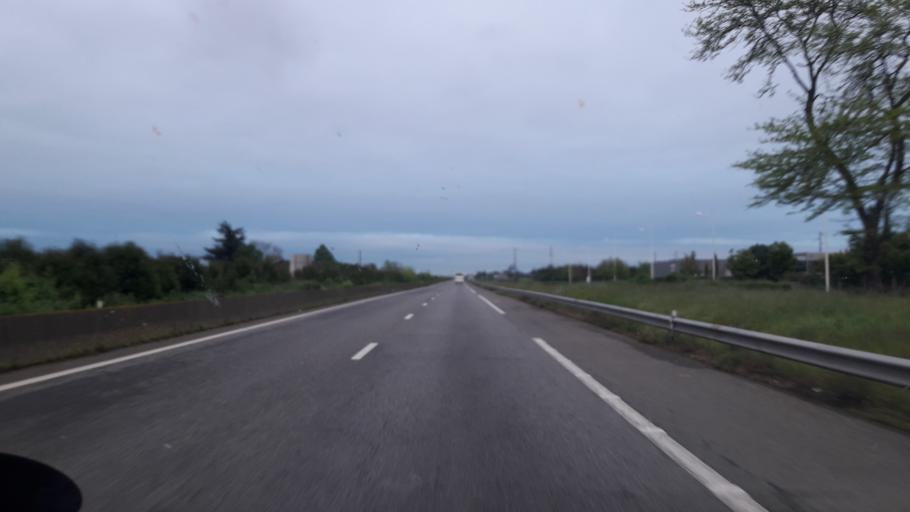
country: FR
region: Midi-Pyrenees
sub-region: Departement de la Haute-Garonne
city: Carbonne
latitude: 43.3142
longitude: 1.2075
